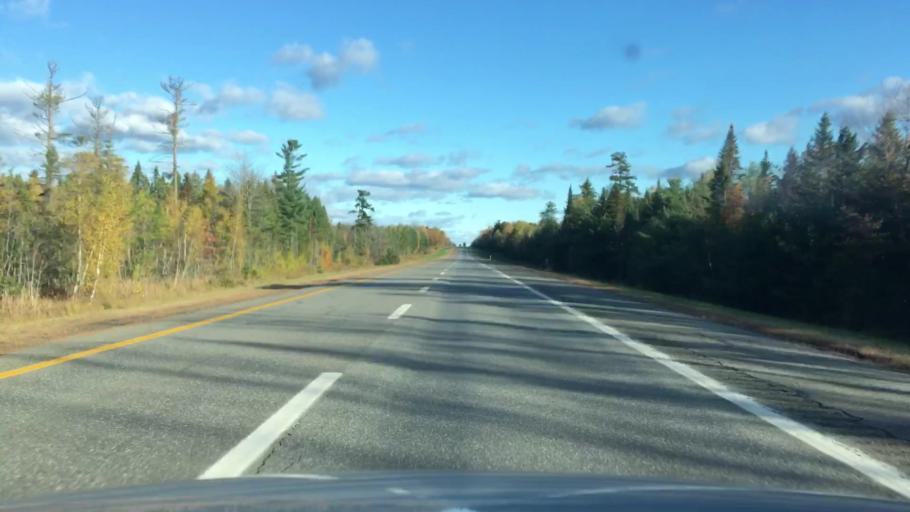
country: US
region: Maine
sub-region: Penobscot County
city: Greenbush
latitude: 45.0612
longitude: -68.6885
